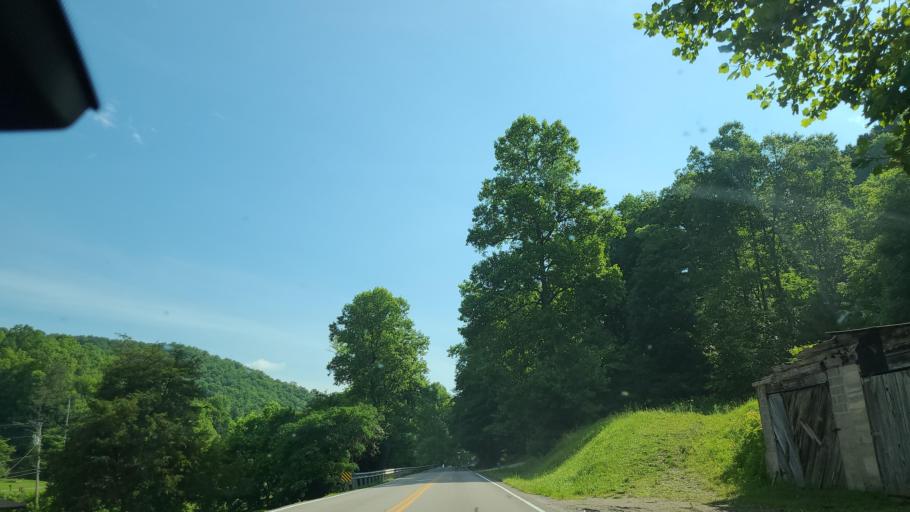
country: US
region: Kentucky
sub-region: Bell County
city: Pineville
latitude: 36.7158
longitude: -83.8162
